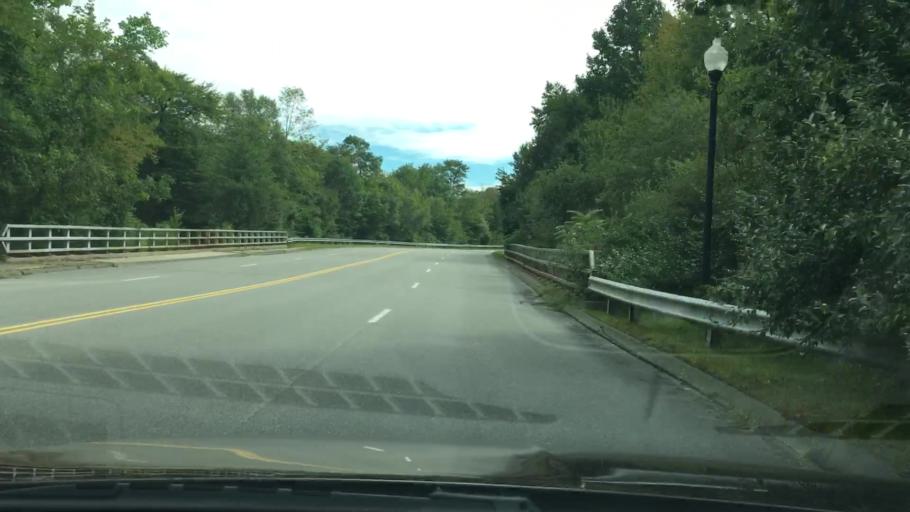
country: US
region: Connecticut
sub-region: Middlesex County
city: Westbrook Center
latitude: 41.2900
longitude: -72.4421
